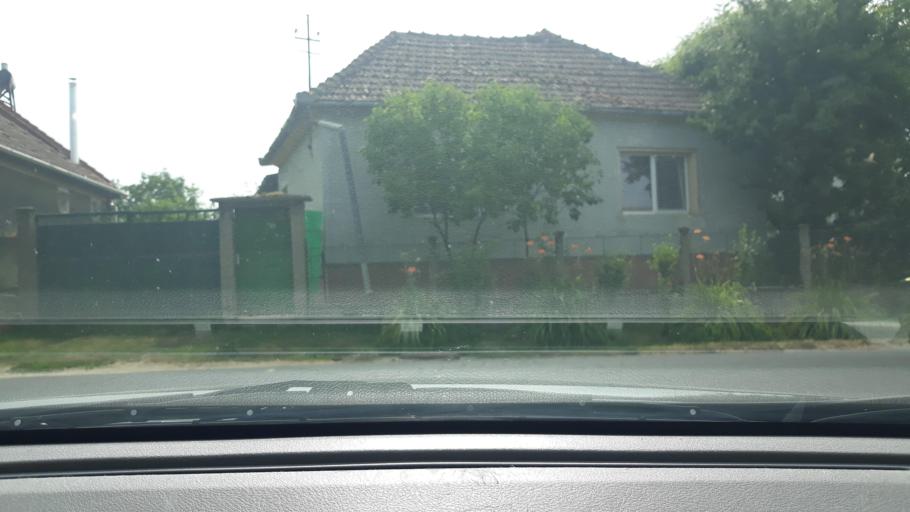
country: RO
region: Bihor
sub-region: Comuna Chislaz
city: Misca
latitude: 47.2644
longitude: 22.2554
